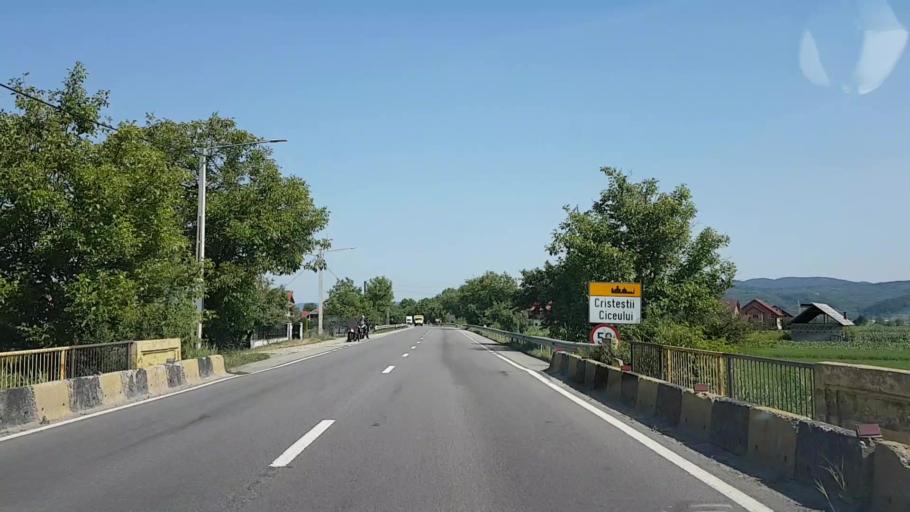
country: RO
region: Bistrita-Nasaud
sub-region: Comuna Uriu
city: Cristestii Ciceului
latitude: 47.1969
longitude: 24.0792
